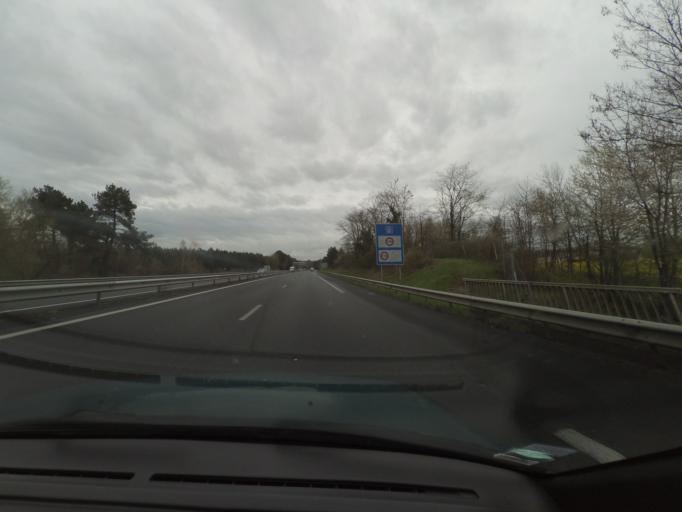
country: FR
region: Pays de la Loire
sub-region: Departement de Maine-et-Loire
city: Seiches-sur-le-Loir
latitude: 47.5506
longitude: -0.3365
